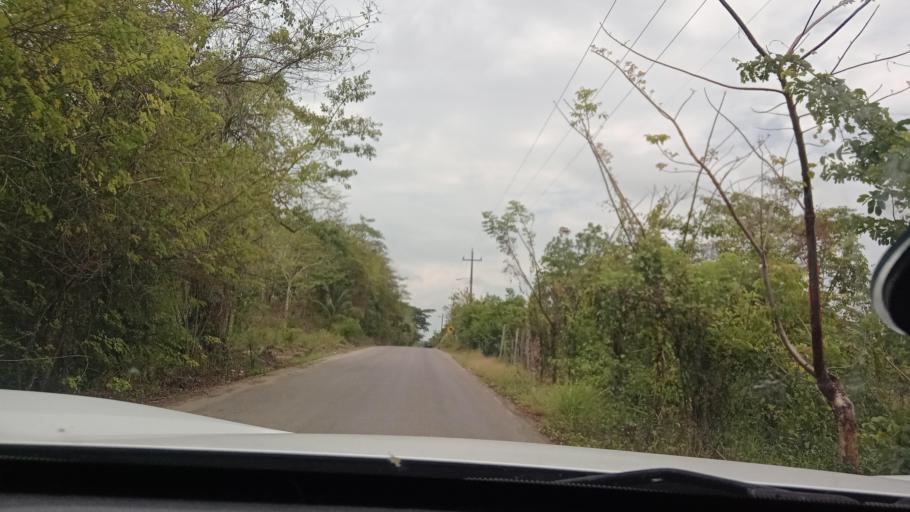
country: MX
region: Tabasco
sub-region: Huimanguillo
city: Francisco Rueda
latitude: 17.5866
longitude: -94.0926
